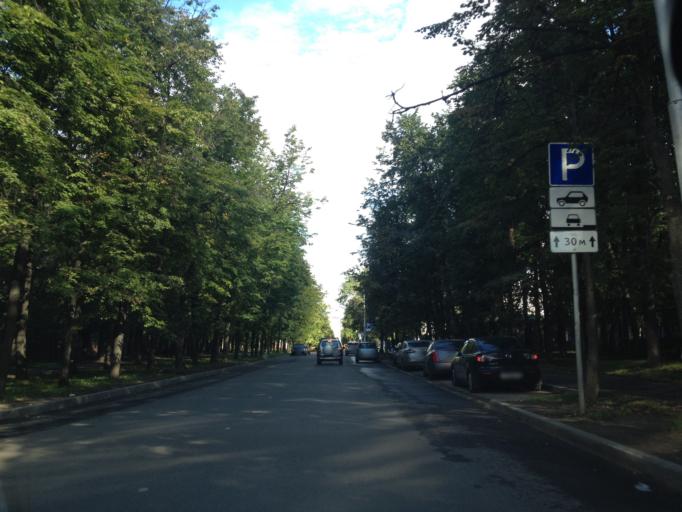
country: RU
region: Moskovskaya
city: Izmaylovo
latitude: 55.7977
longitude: 37.8054
